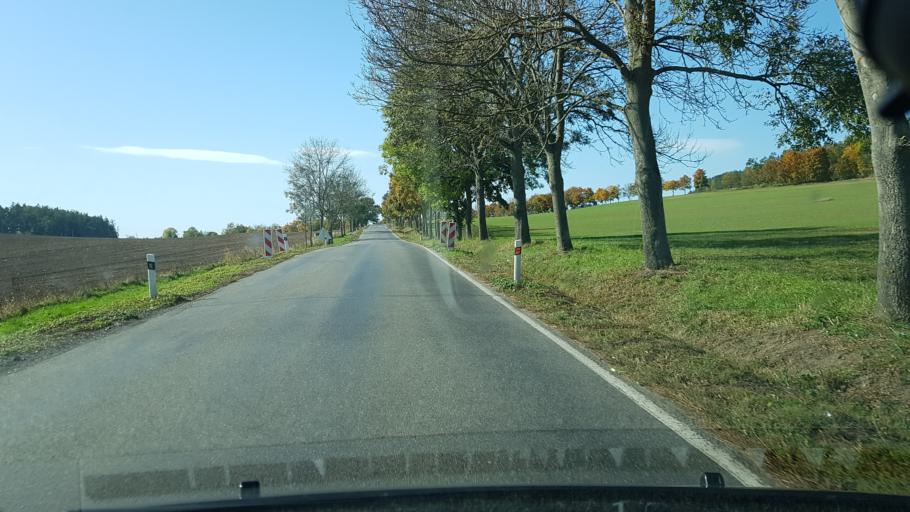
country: CZ
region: Jihocesky
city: Radomysl
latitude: 49.2983
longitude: 13.9988
